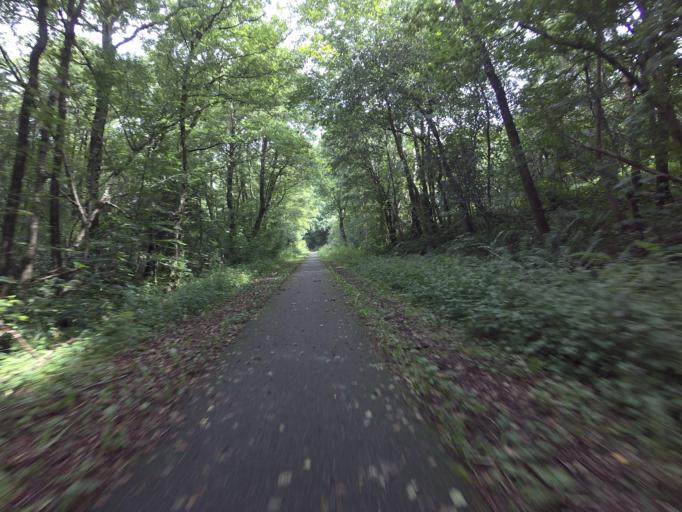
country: DK
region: Central Jutland
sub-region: Favrskov Kommune
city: Hammel
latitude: 56.3163
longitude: 9.8665
